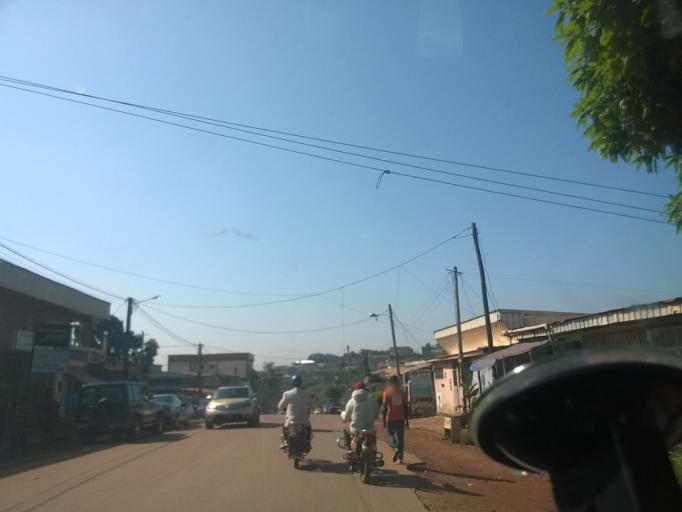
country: CM
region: Centre
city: Yaounde
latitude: 3.8346
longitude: 11.4831
